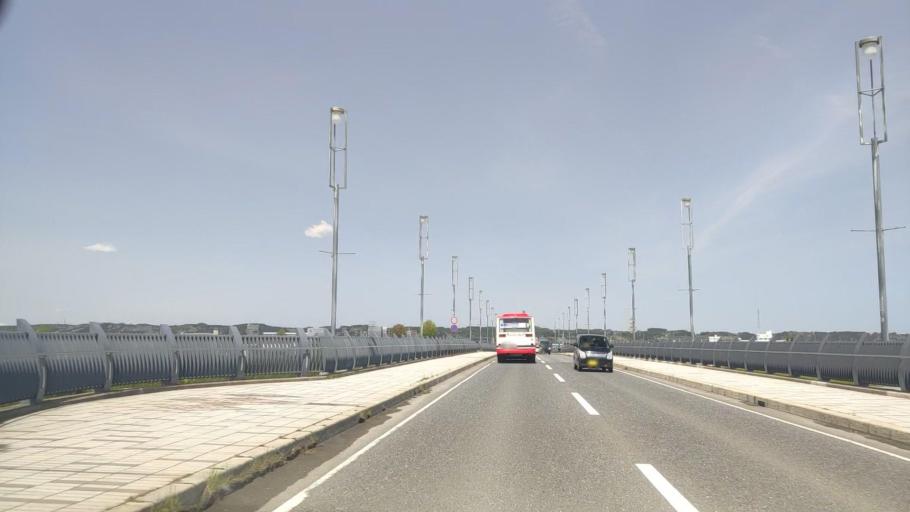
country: JP
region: Aomori
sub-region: Hachinohe Shi
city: Uchimaru
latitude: 40.5007
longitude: 141.4433
